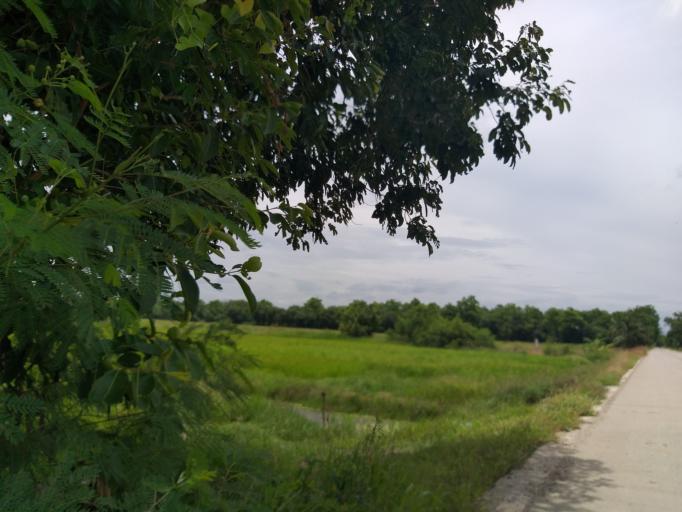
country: TH
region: Pathum Thani
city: Ban Lam Luk Ka
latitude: 14.0300
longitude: 100.8659
